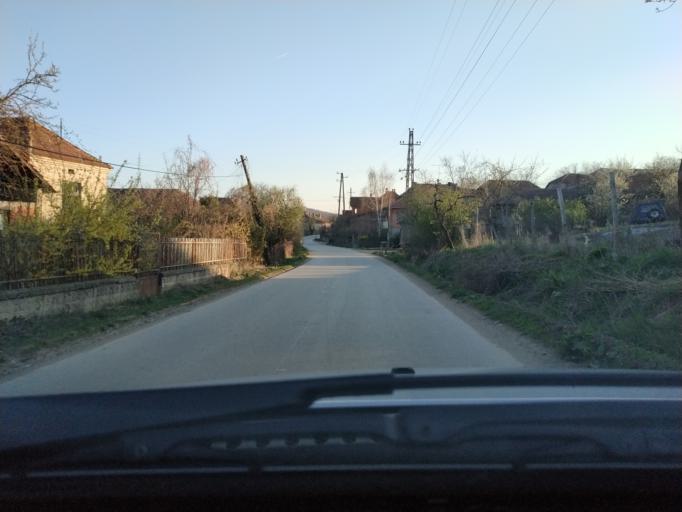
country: RS
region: Central Serbia
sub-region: Nisavski Okrug
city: Aleksinac
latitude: 43.5068
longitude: 21.7962
